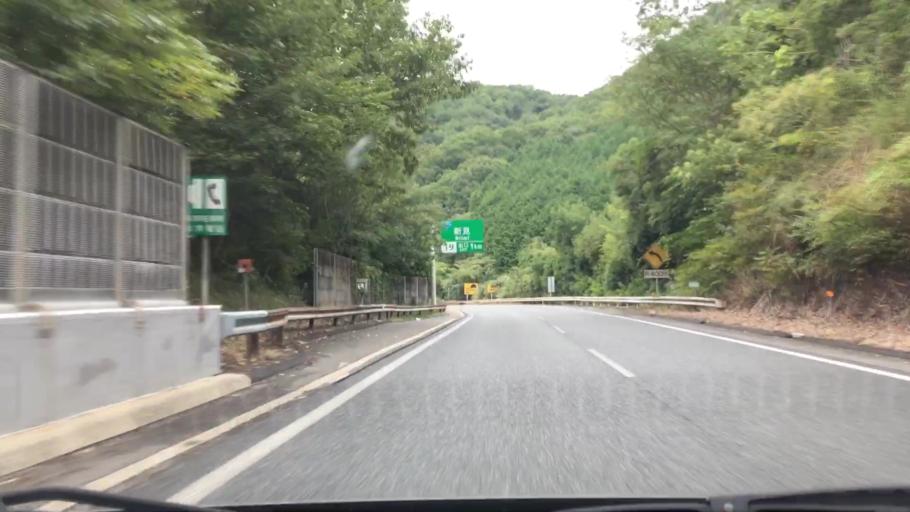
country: JP
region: Okayama
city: Niimi
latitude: 34.9914
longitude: 133.4595
